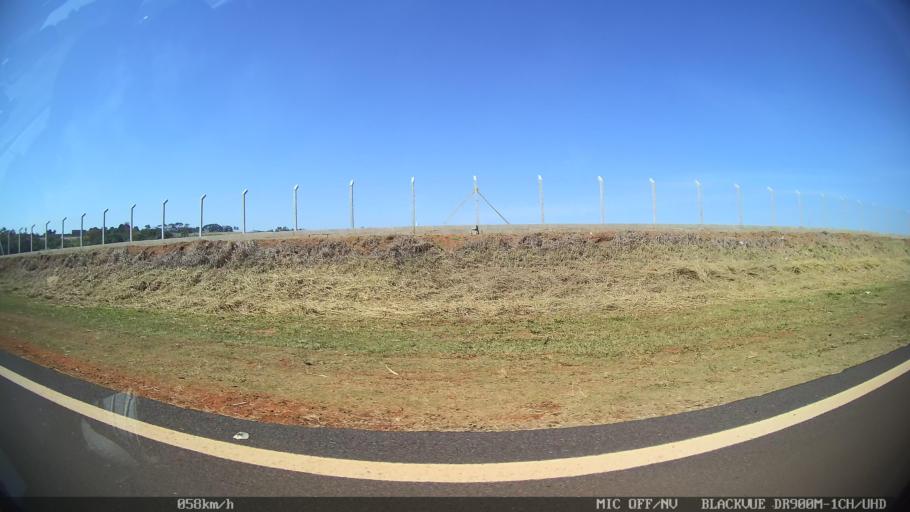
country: BR
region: Sao Paulo
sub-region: Batatais
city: Batatais
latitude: -20.8739
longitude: -47.6058
